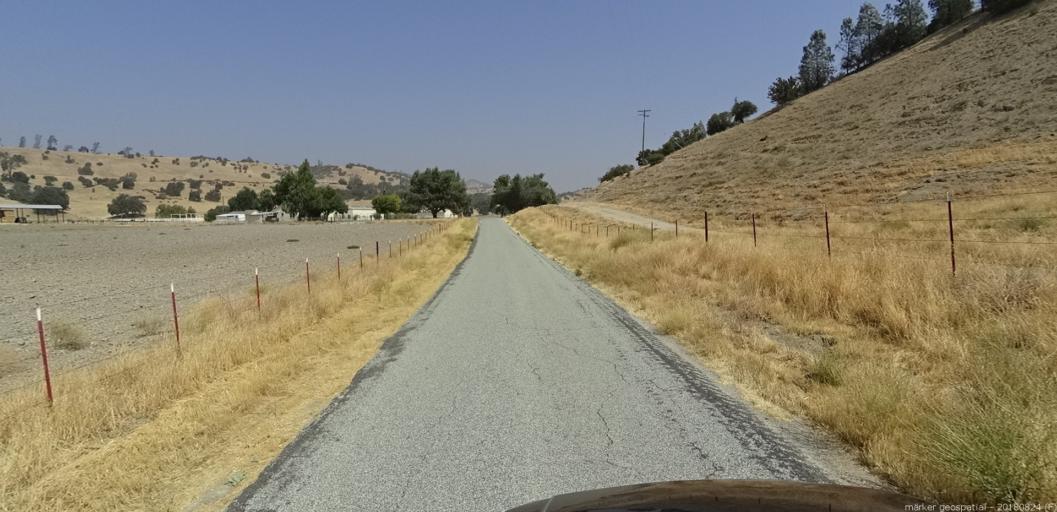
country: US
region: California
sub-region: San Luis Obispo County
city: San Miguel
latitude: 35.9542
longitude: -120.6550
